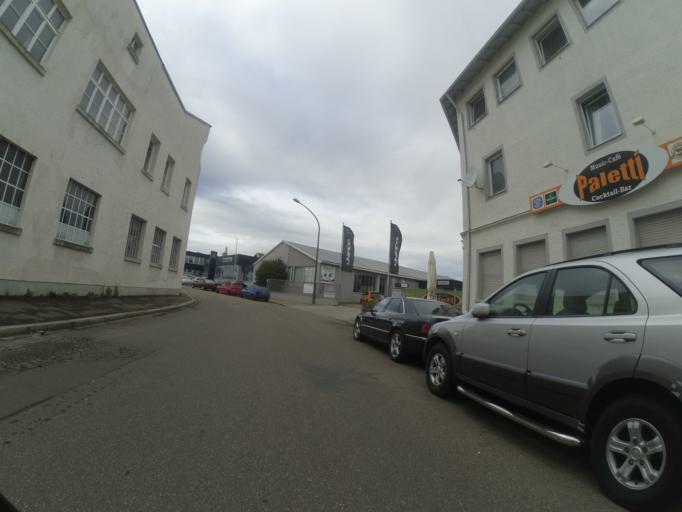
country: DE
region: Bavaria
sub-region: Swabia
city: Neu-Ulm
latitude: 48.3972
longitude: 10.0137
